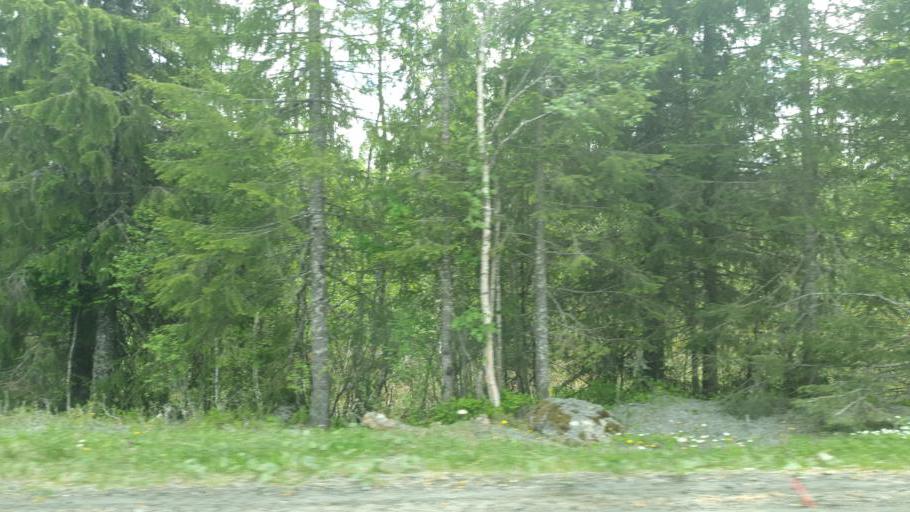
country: NO
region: Nord-Trondelag
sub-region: Leksvik
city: Leksvik
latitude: 63.6919
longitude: 10.4230
